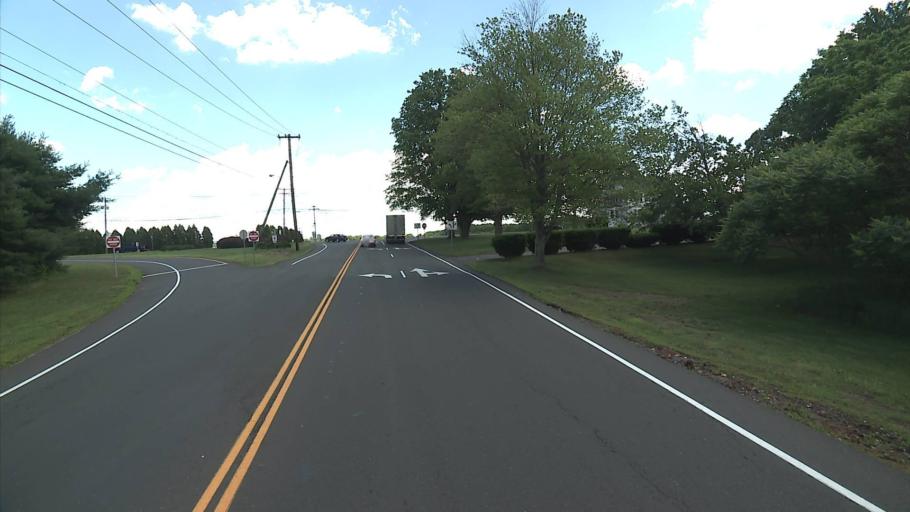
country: US
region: Connecticut
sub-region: Hartford County
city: Hazardville
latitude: 42.0145
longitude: -72.5147
